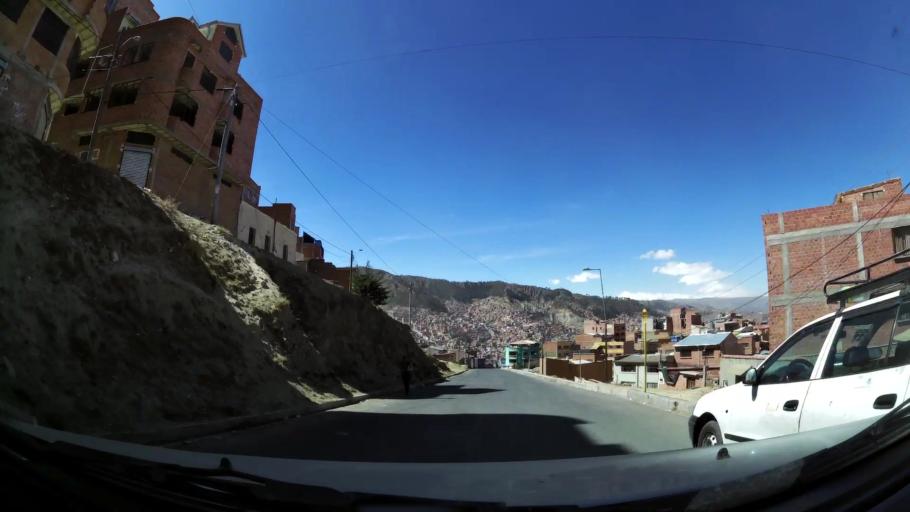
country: BO
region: La Paz
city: La Paz
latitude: -16.4890
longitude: -68.1535
